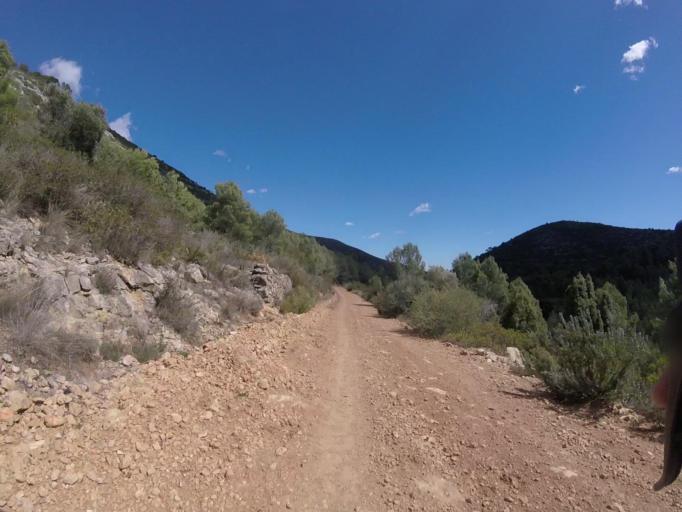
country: ES
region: Valencia
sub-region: Provincia de Castello
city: Orpesa/Oropesa del Mar
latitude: 40.1660
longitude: 0.1215
